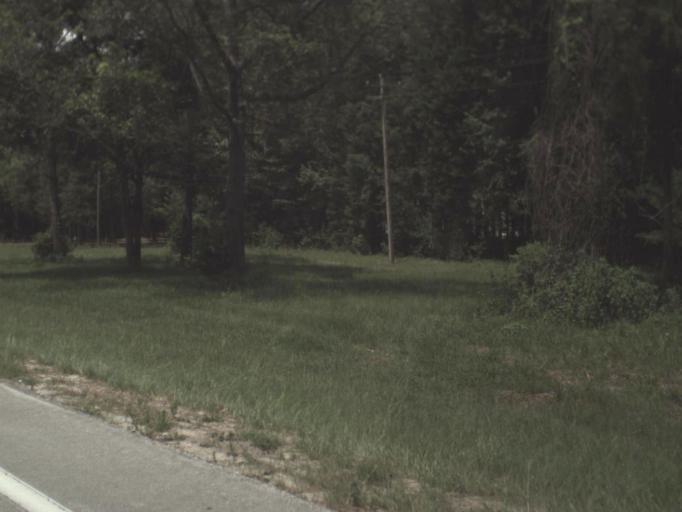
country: US
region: Florida
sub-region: Alachua County
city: Newberry
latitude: 29.7350
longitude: -82.6072
